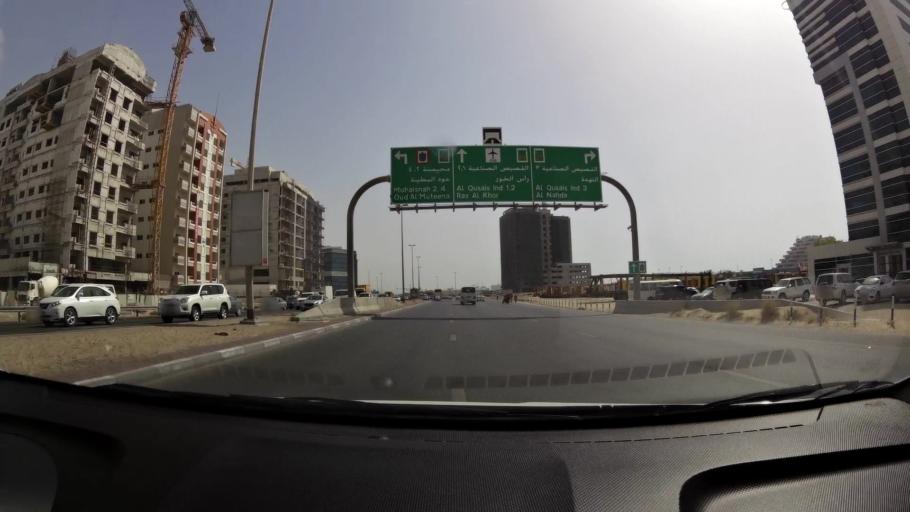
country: AE
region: Ash Shariqah
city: Sharjah
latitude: 25.2905
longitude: 55.4028
